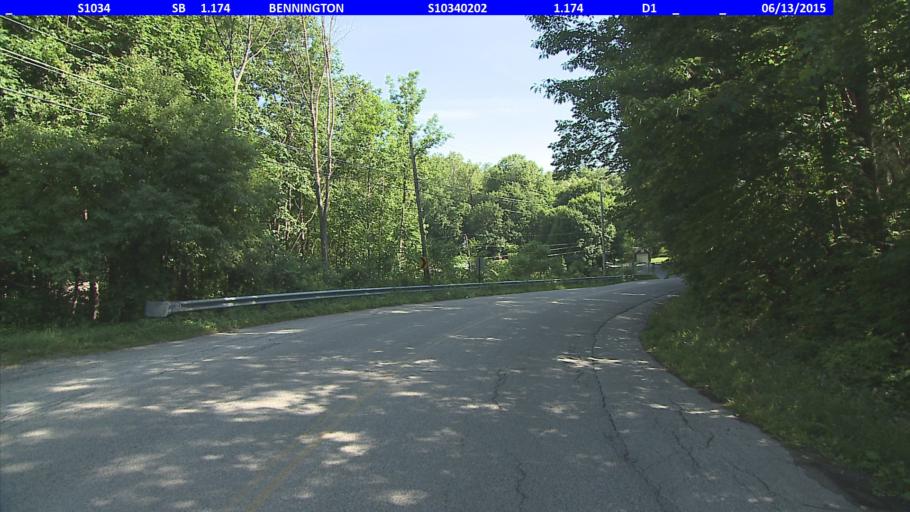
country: US
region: Vermont
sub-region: Bennington County
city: Bennington
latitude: 42.8681
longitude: -73.2091
